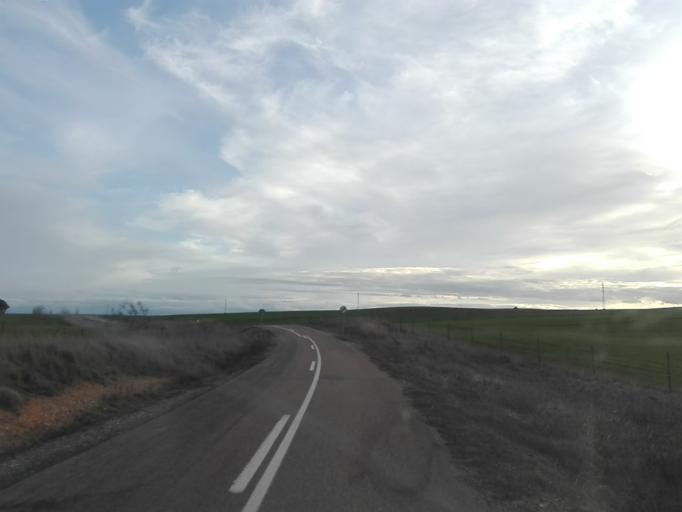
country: ES
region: Extremadura
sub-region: Provincia de Badajoz
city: Usagre
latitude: 38.4106
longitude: -6.1755
